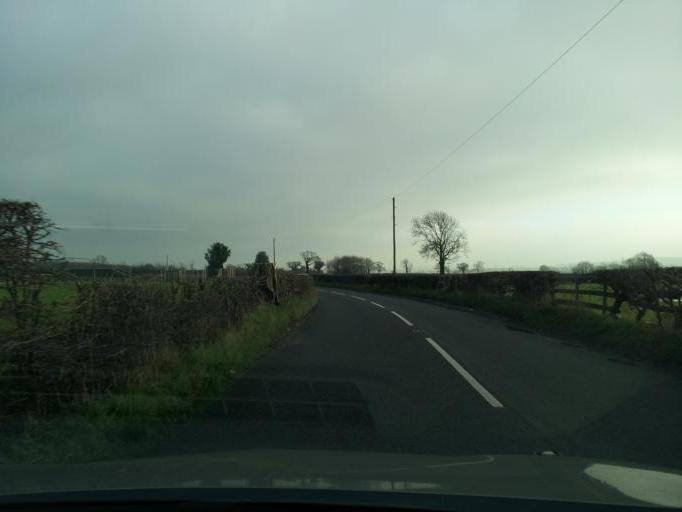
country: GB
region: England
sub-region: Derbyshire
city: Rodsley
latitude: 52.8807
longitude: -1.7507
